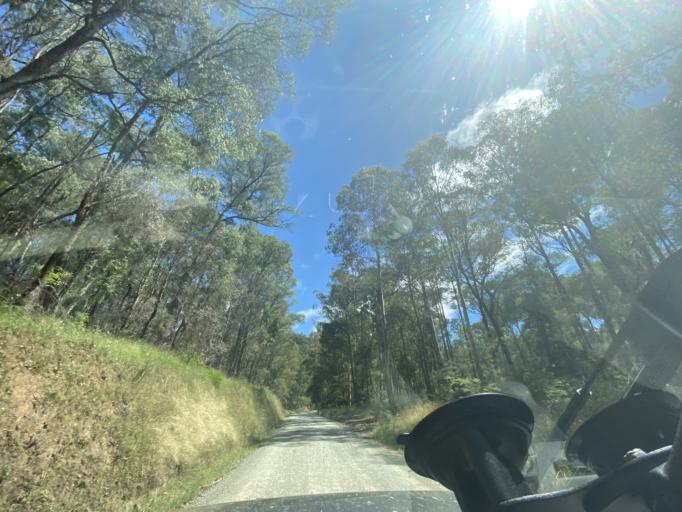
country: AU
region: Victoria
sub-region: Yarra Ranges
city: Millgrove
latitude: -37.5273
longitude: 146.0020
